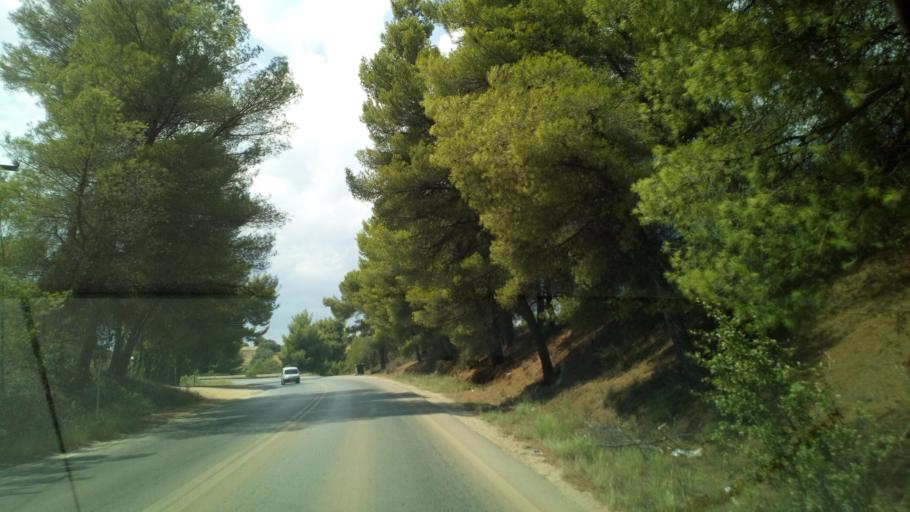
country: GR
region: Central Macedonia
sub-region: Nomos Chalkidikis
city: Nikiti
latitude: 40.2297
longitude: 23.6309
